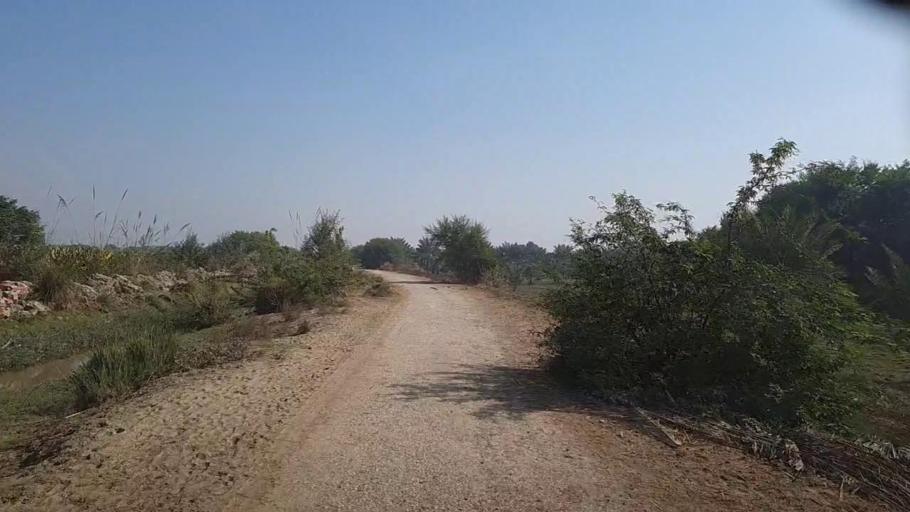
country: PK
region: Sindh
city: Bozdar
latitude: 27.1917
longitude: 68.6234
